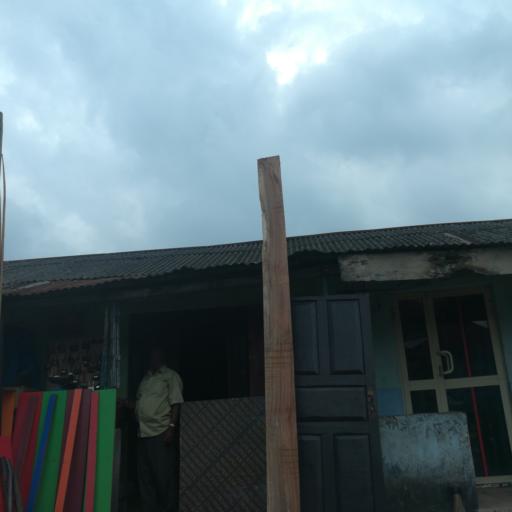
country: NG
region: Rivers
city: Port Harcourt
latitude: 4.8075
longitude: 7.0500
